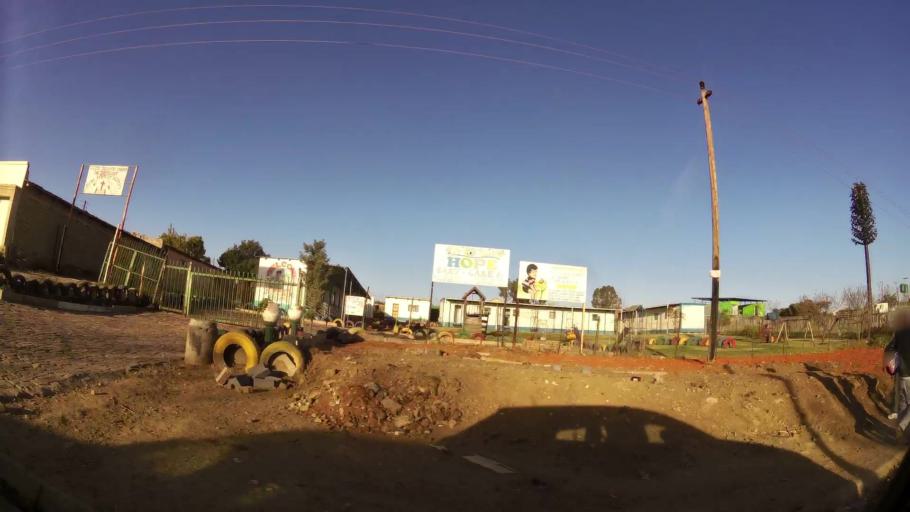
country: ZA
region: Gauteng
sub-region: City of Johannesburg Metropolitan Municipality
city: Diepsloot
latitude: -25.9409
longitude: 28.0140
